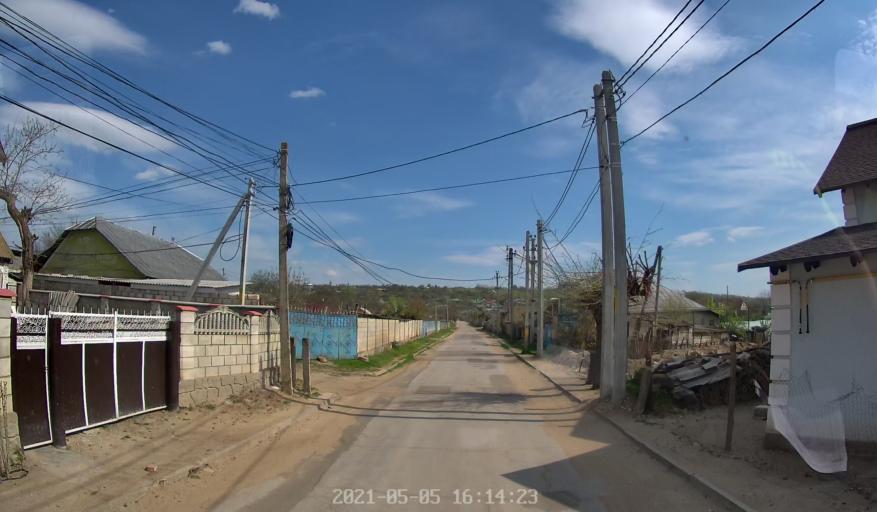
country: MD
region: Criuleni
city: Criuleni
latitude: 47.1377
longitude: 29.2004
